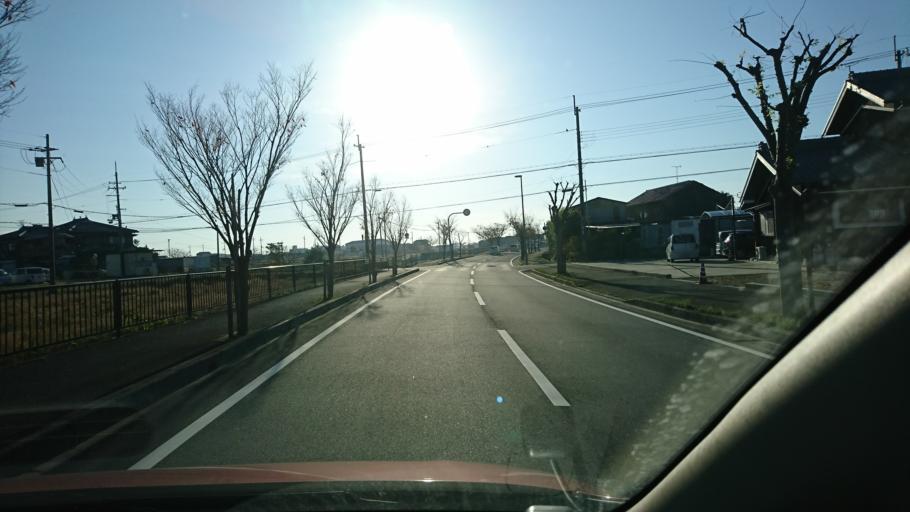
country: JP
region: Hyogo
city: Miki
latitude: 34.7711
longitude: 134.9100
